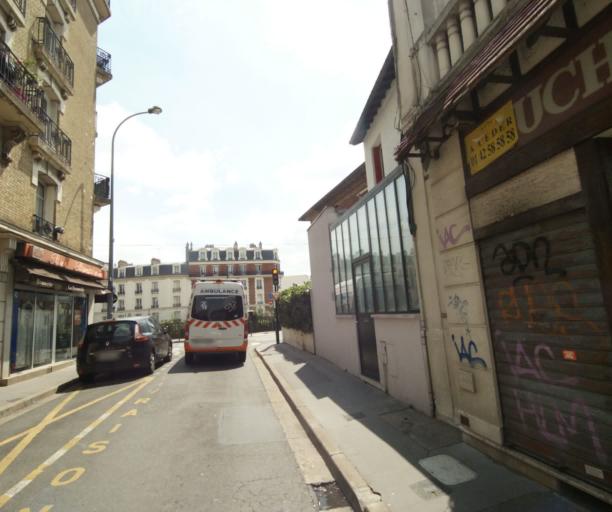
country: FR
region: Ile-de-France
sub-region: Departement des Hauts-de-Seine
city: La Garenne-Colombes
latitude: 48.9103
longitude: 2.2402
